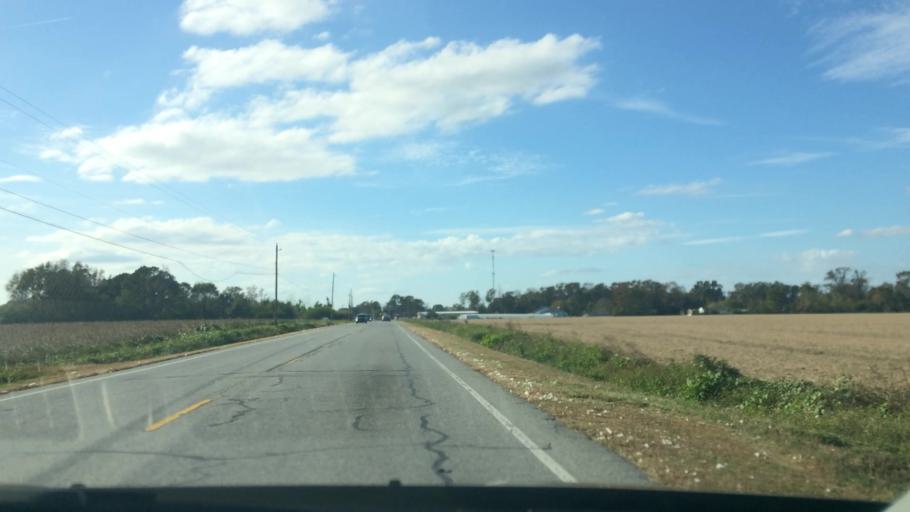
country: US
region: North Carolina
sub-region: Greene County
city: Snow Hill
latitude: 35.4392
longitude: -77.7848
